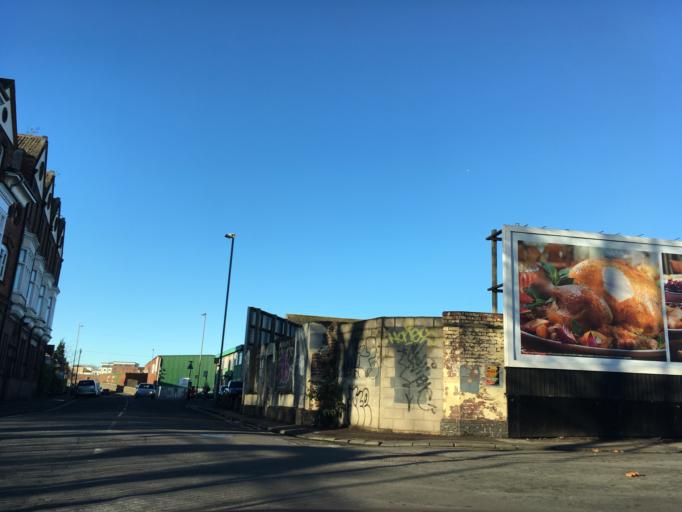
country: GB
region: England
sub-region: Bristol
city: Bristol
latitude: 51.4525
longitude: -2.5743
